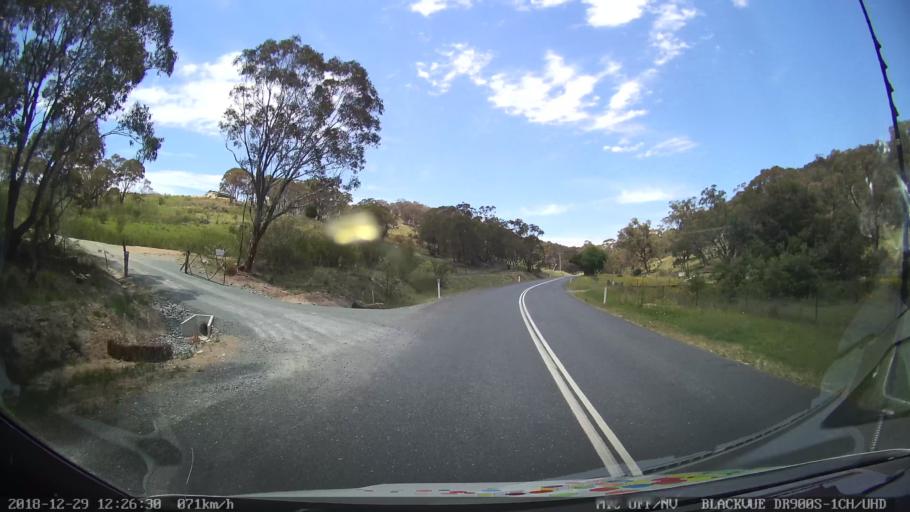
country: AU
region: New South Wales
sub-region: Queanbeyan
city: Queanbeyan
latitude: -35.4660
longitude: 149.2240
